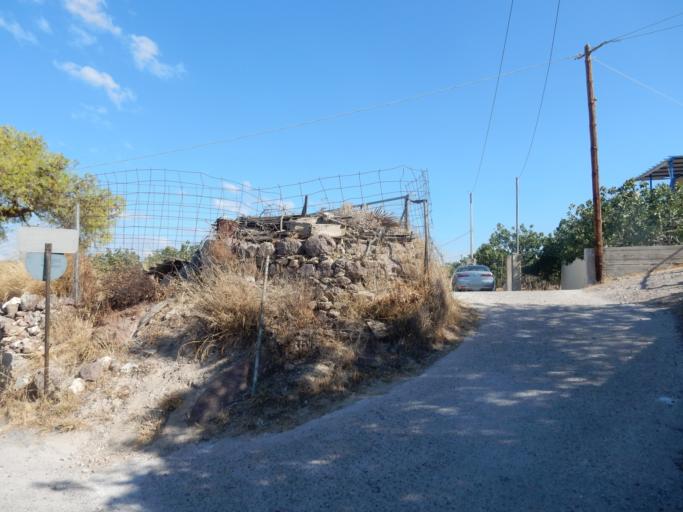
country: GR
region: Attica
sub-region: Nomos Piraios
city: Aegina
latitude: 37.7294
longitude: 23.4445
